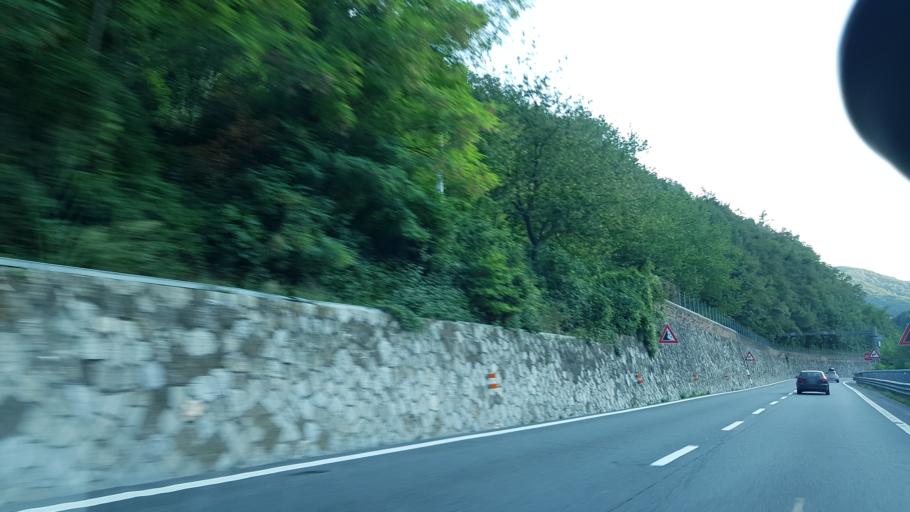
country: IT
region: Liguria
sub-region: Provincia di Genova
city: Ronco Scrivia
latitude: 44.6214
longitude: 8.9507
